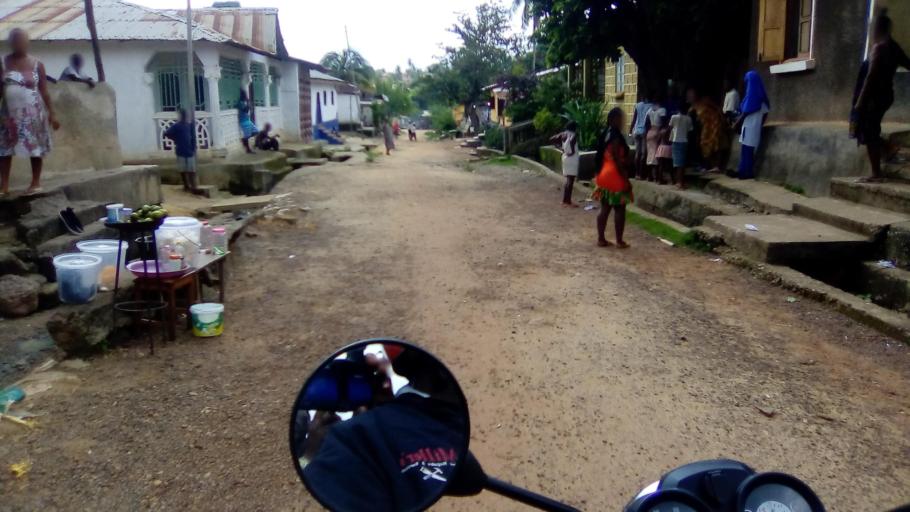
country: SL
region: Southern Province
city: Bo
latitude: 7.9628
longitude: -11.7331
